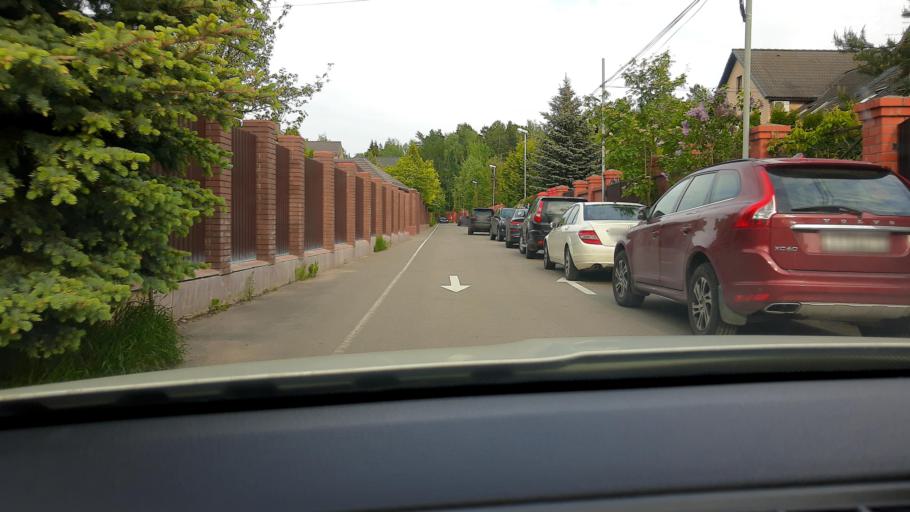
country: RU
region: Moskovskaya
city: Vatutinki
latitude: 55.5114
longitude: 37.3792
